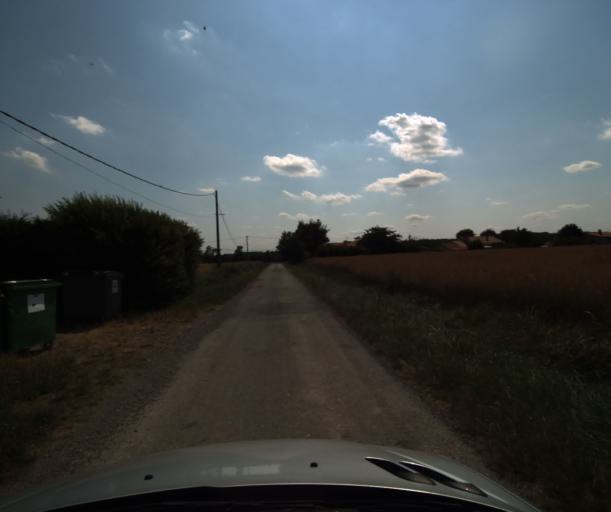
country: FR
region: Midi-Pyrenees
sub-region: Departement de la Haute-Garonne
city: Saint-Lys
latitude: 43.5277
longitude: 1.1655
